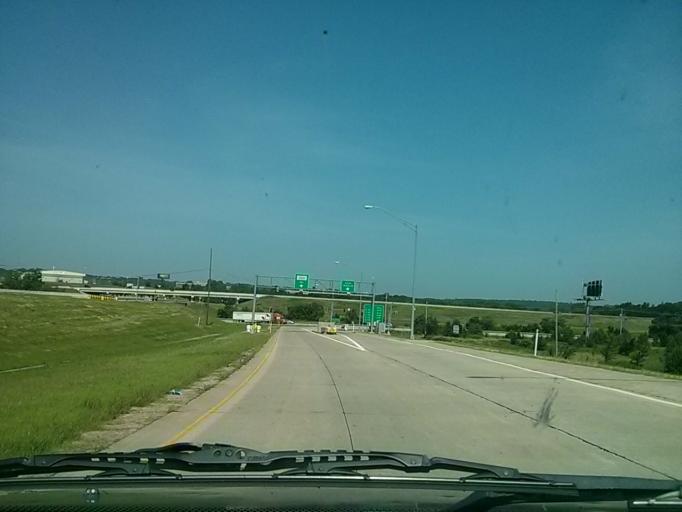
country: US
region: Oklahoma
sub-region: Creek County
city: Sapulpa
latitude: 36.0294
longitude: -96.0858
